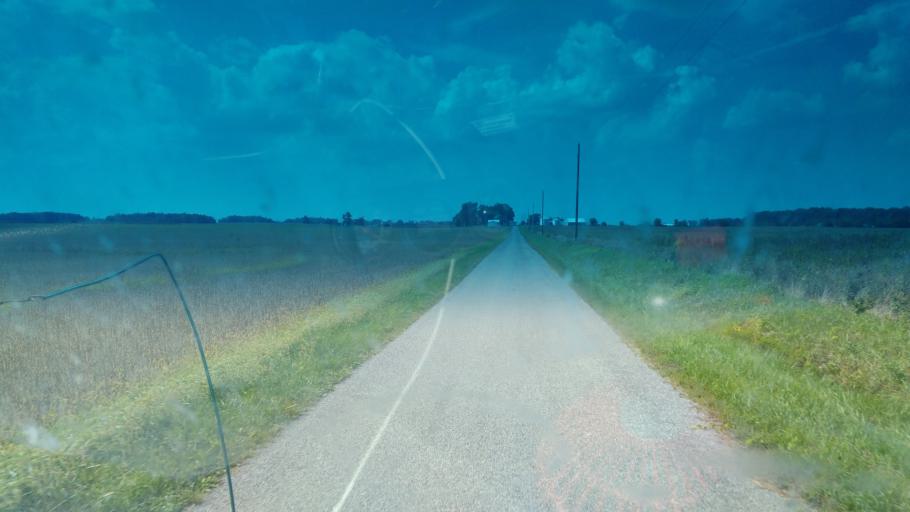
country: US
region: Ohio
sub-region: Hardin County
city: Ada
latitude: 40.6819
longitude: -83.8700
